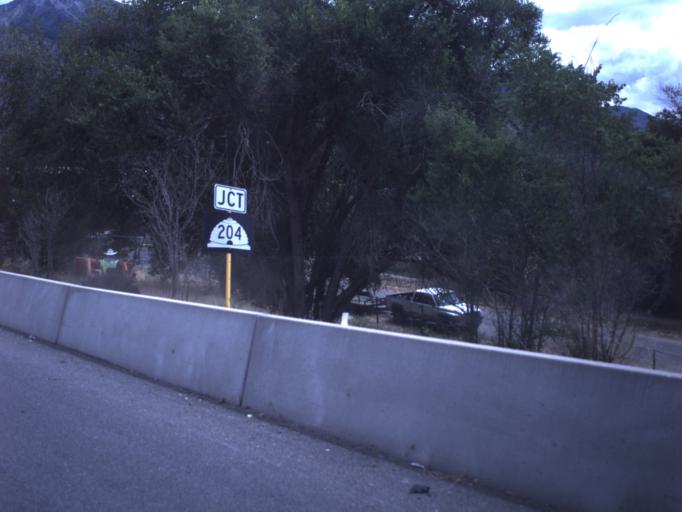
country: US
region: Utah
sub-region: Weber County
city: Ogden
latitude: 41.2078
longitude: -111.9824
